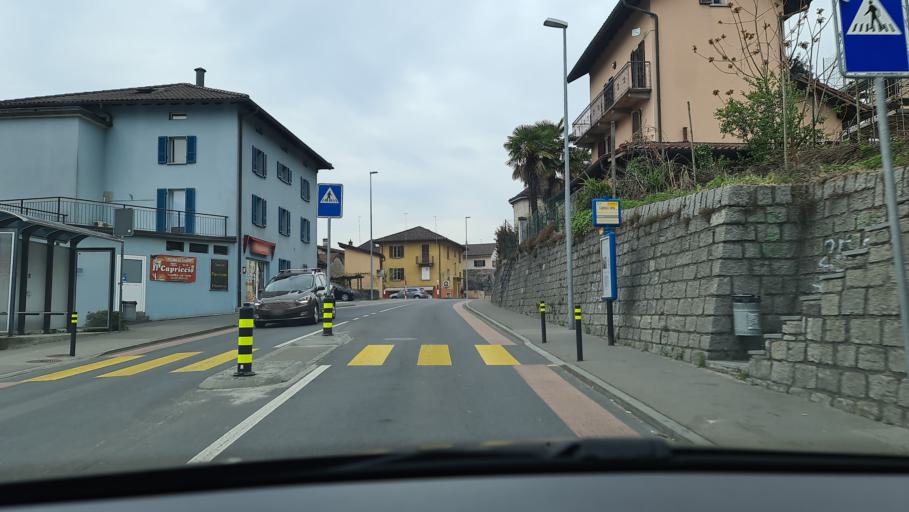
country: CH
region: Ticino
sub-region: Locarno District
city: Cugnasco
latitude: 46.1753
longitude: 8.9194
